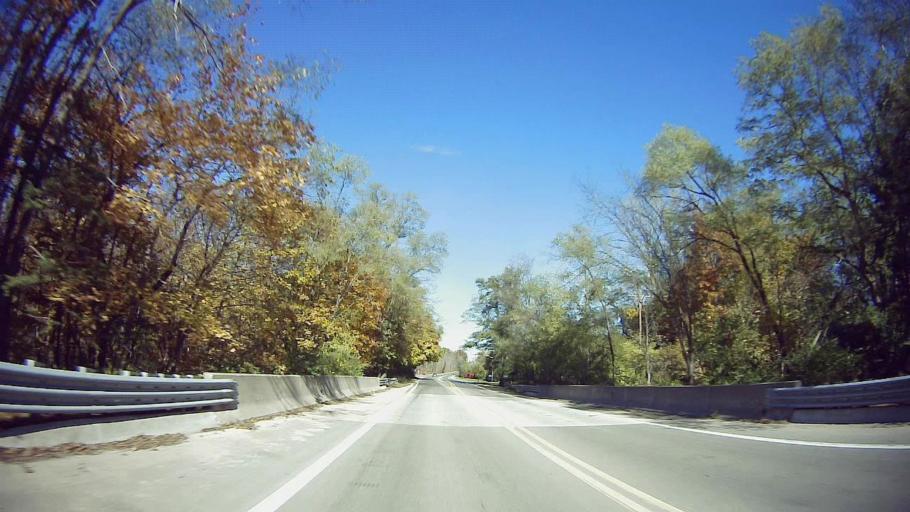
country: US
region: Michigan
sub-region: Oakland County
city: Bingham Farms
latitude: 42.5099
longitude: -83.2623
